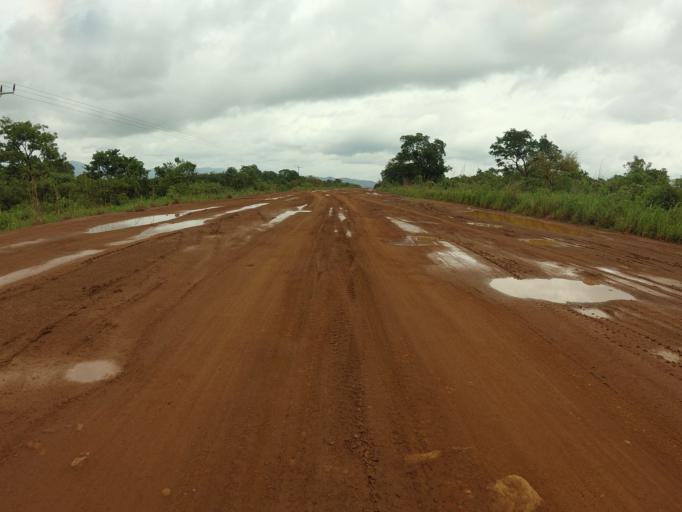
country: GH
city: Kpandae
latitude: 8.3100
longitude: 0.4836
